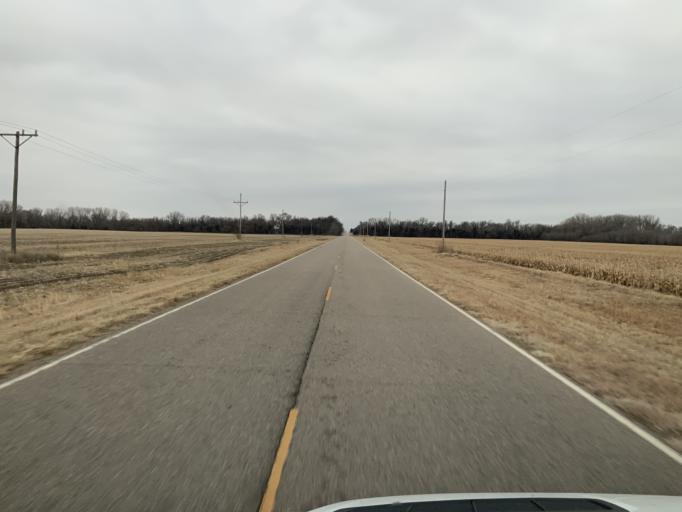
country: US
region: Kansas
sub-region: Reno County
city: South Hutchinson
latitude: 37.9394
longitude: -98.0869
